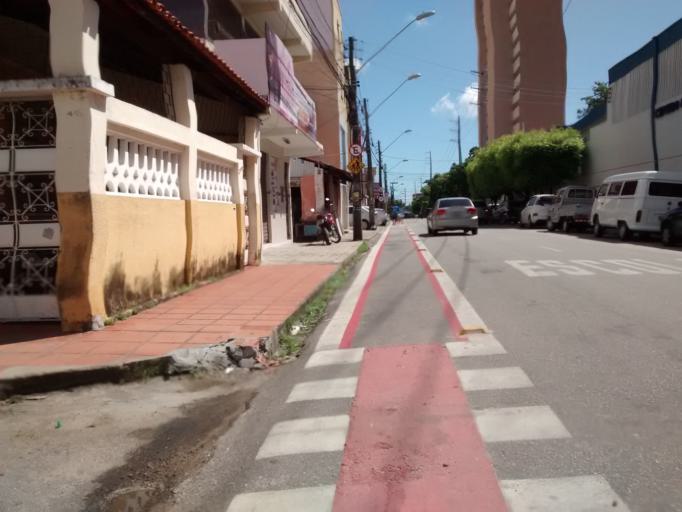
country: BR
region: Ceara
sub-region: Fortaleza
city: Fortaleza
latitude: -3.7372
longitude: -38.5570
